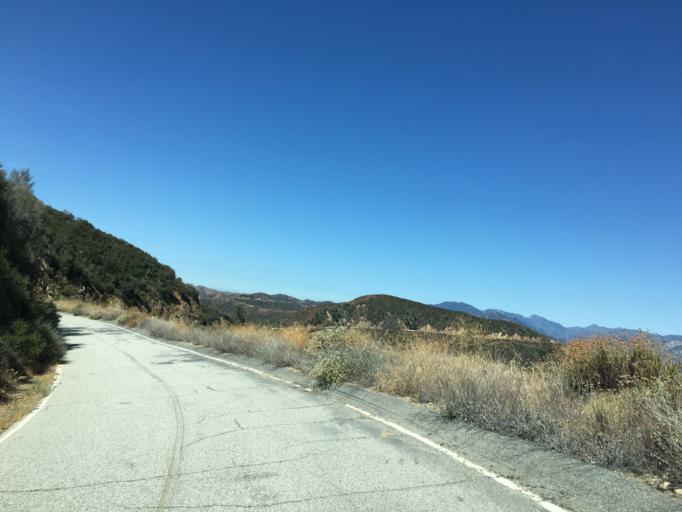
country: US
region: California
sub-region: San Bernardino County
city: San Antonio Heights
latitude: 34.2211
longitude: -117.7405
